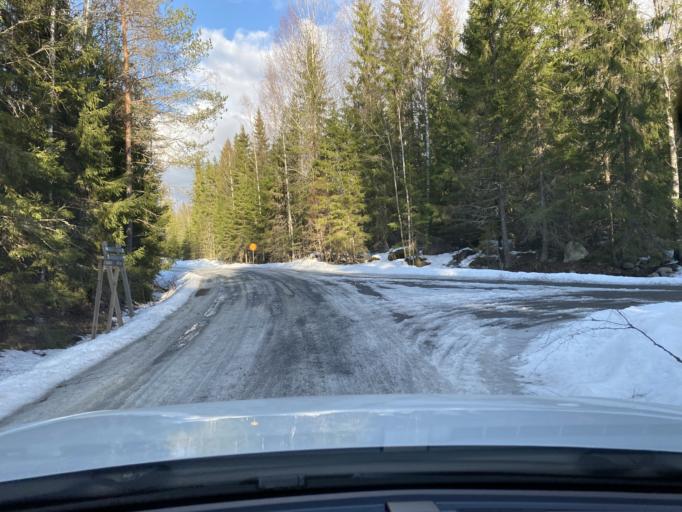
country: FI
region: Pirkanmaa
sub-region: Lounais-Pirkanmaa
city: Mouhijaervi
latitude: 61.4614
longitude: 22.9580
